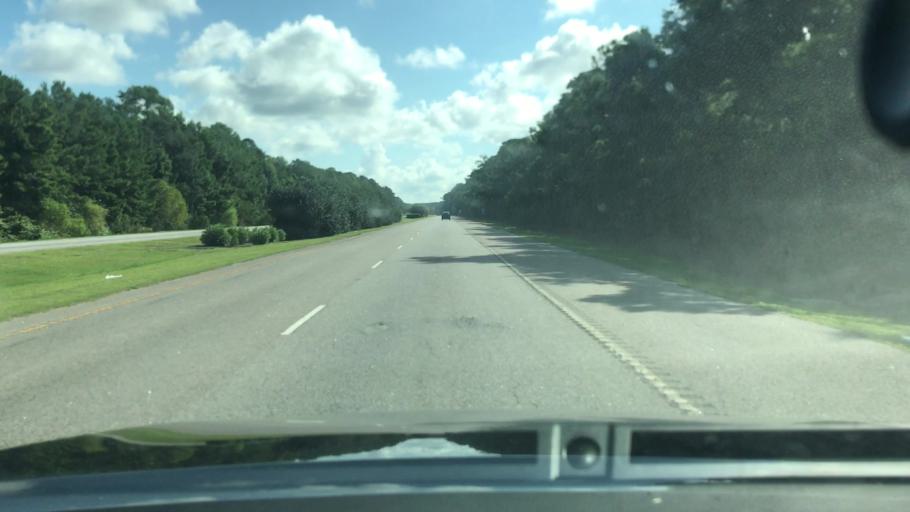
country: US
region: South Carolina
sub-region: Beaufort County
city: Hilton Head Island
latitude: 32.1983
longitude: -80.7573
